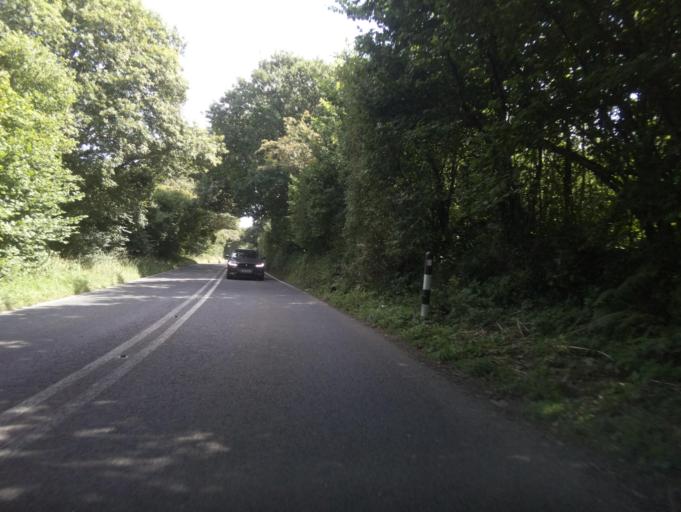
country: GB
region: England
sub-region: Cornwall
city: Saltash
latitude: 50.4275
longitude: -4.2546
